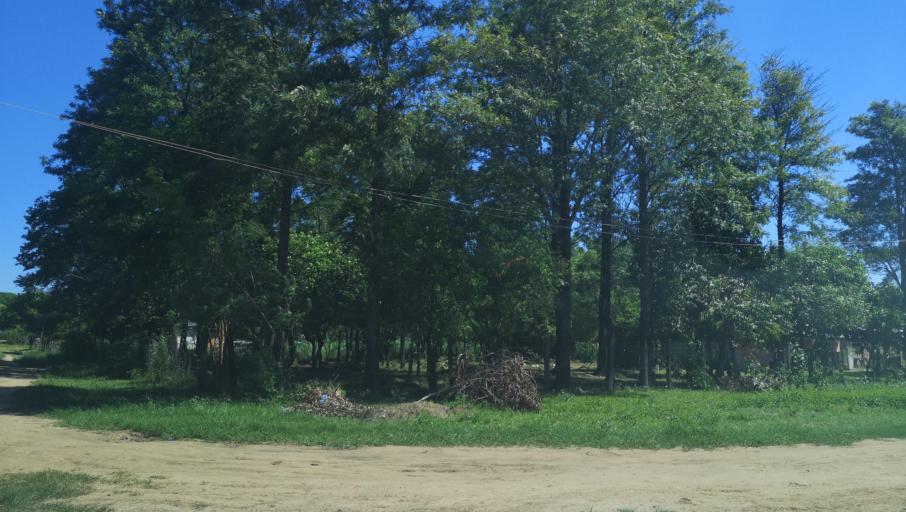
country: PY
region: Caaguazu
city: Carayao
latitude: -25.2046
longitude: -56.3959
